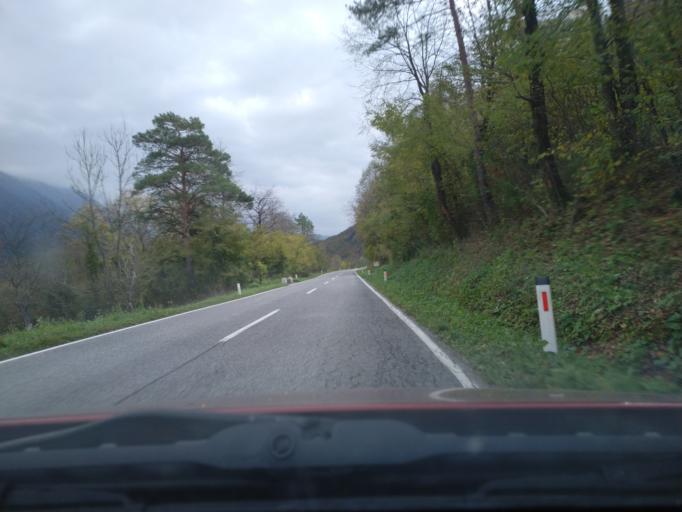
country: SI
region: Bovec
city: Bovec
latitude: 46.2887
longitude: 13.5057
